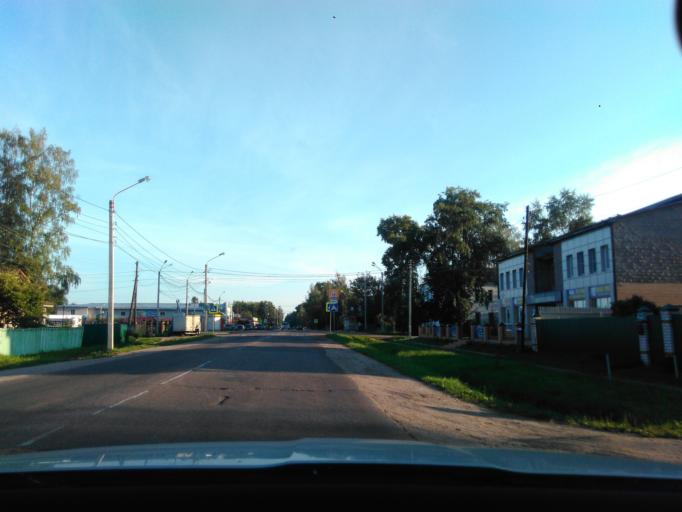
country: RU
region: Tverskaya
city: Konakovo
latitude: 56.6957
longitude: 36.7658
